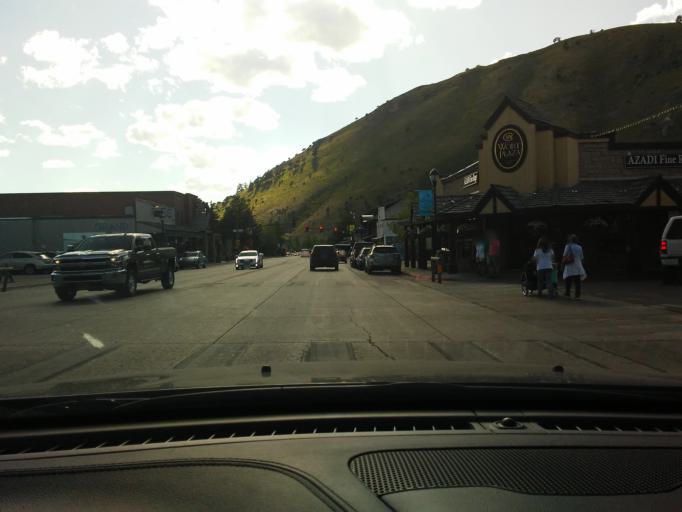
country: US
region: Wyoming
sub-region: Teton County
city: Jackson
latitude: 43.4797
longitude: -110.7635
